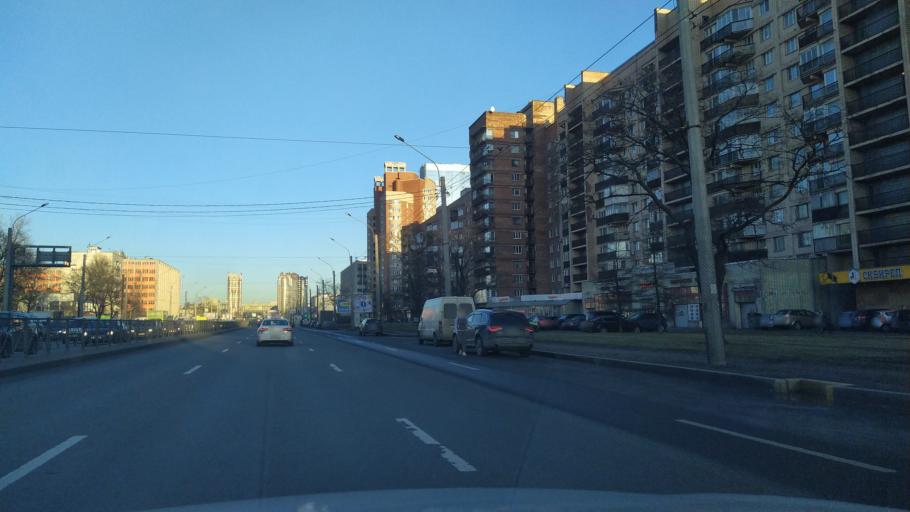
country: RU
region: St.-Petersburg
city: Avtovo
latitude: 59.8519
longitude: 30.2942
